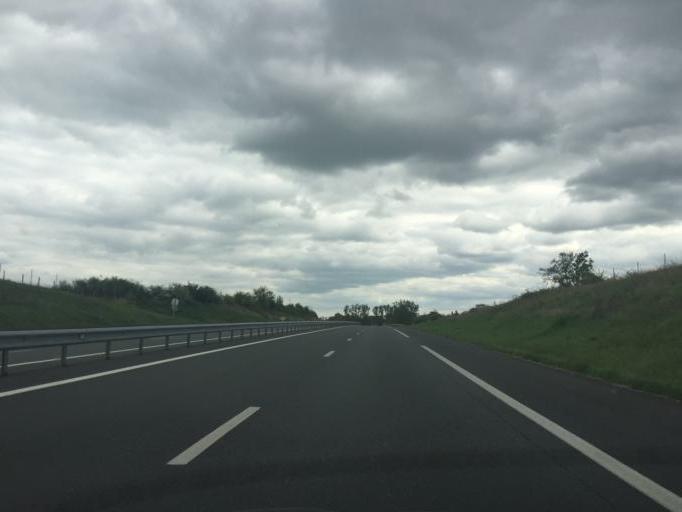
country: FR
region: Rhone-Alpes
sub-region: Departement de la Loire
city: La Pacaudiere
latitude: 46.1752
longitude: 3.8804
